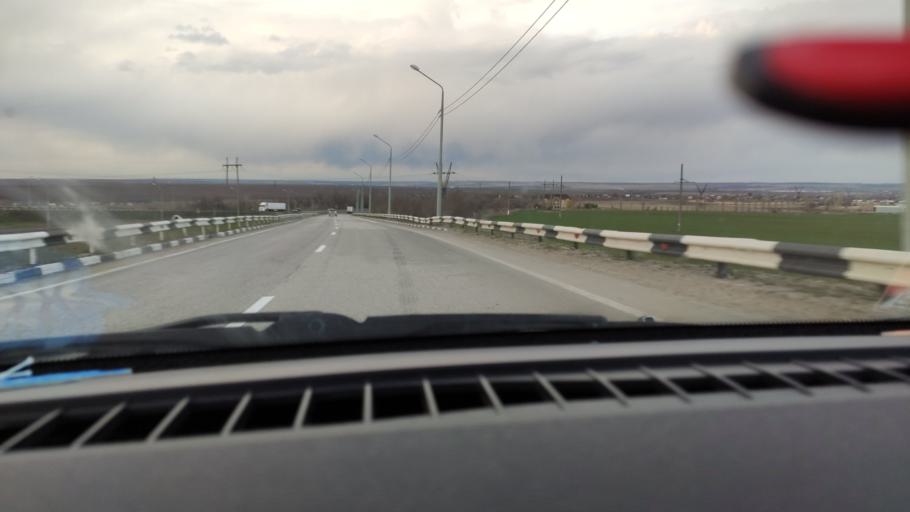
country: RU
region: Saratov
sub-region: Saratovskiy Rayon
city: Saratov
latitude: 51.6745
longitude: 46.0007
